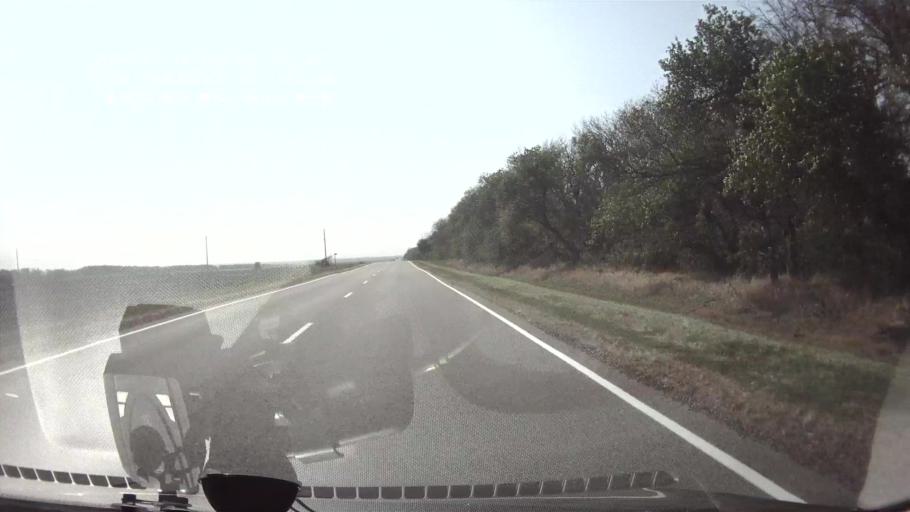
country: RU
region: Krasnodarskiy
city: Dmitriyevskaya
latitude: 45.7854
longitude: 40.7195
